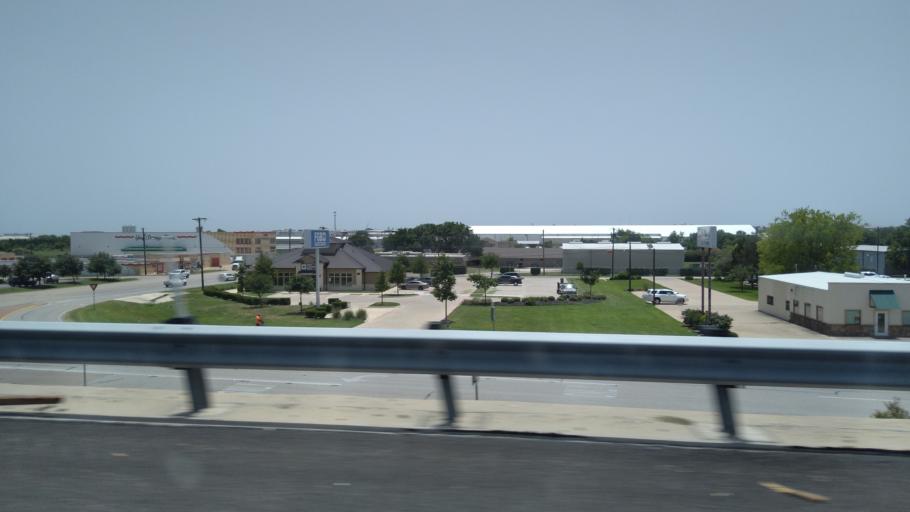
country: US
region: Texas
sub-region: McLennan County
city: Woodway
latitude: 31.5038
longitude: -97.2050
